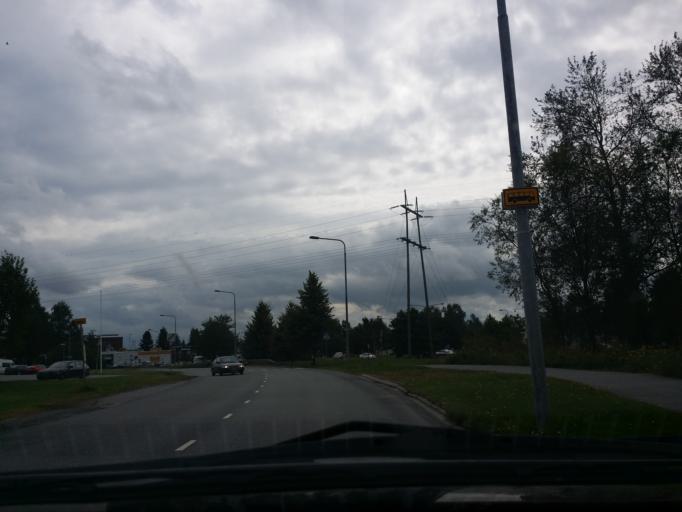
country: FI
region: Satakunta
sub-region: Pori
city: Pori
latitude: 61.4995
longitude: 21.8038
